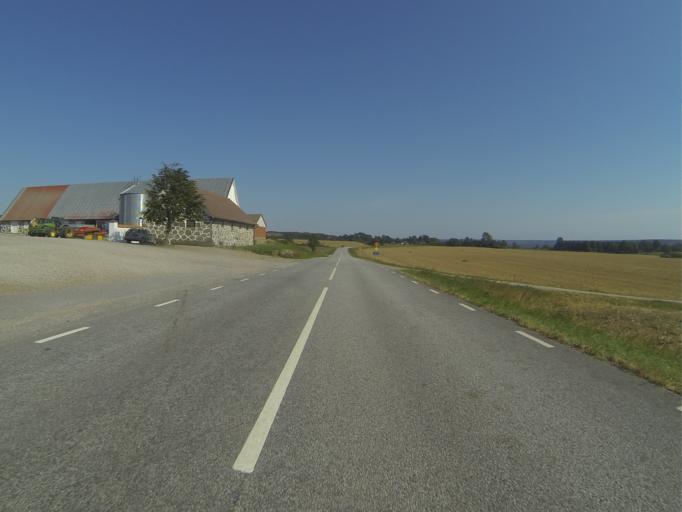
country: SE
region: Skane
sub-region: Hoors Kommun
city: Loberod
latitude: 55.7102
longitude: 13.5498
